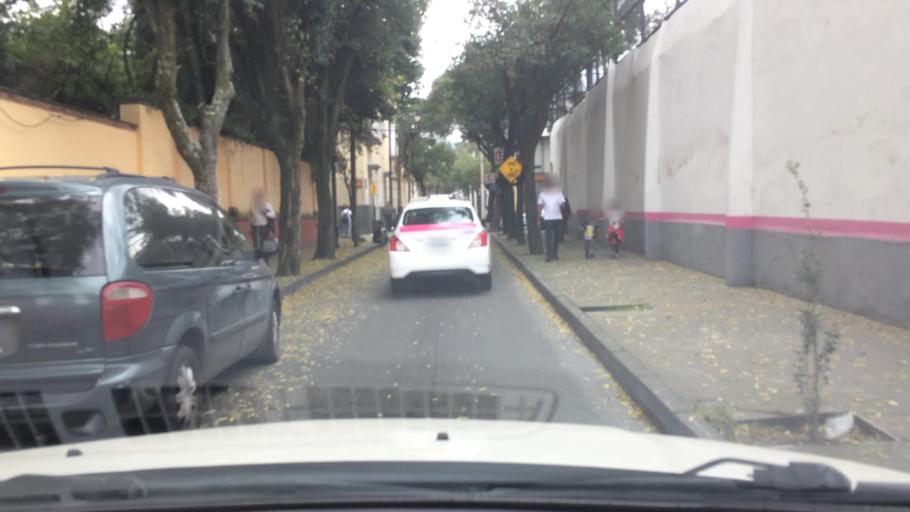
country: MX
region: Mexico City
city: Tlalpan
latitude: 19.2914
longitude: -99.1680
